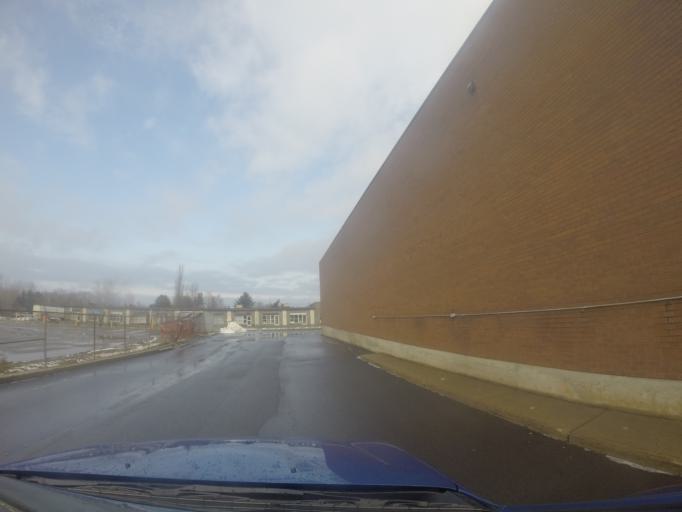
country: CA
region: Ontario
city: Greater Sudbury
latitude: 46.5230
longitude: -80.9306
